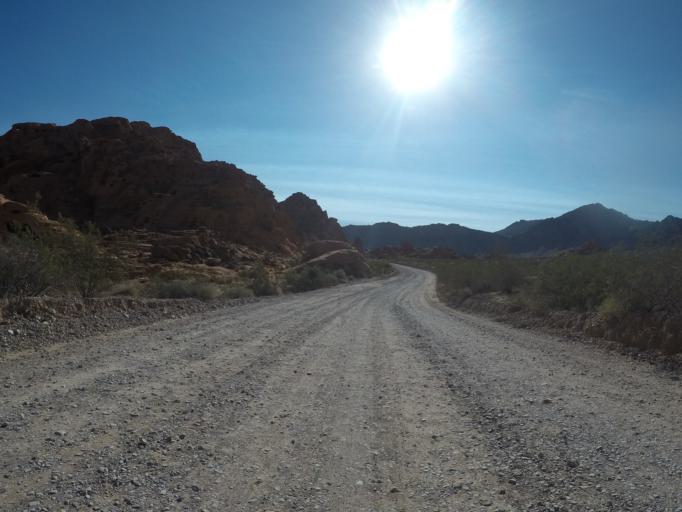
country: US
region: Nevada
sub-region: Clark County
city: Moapa Valley
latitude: 36.4165
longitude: -114.5597
